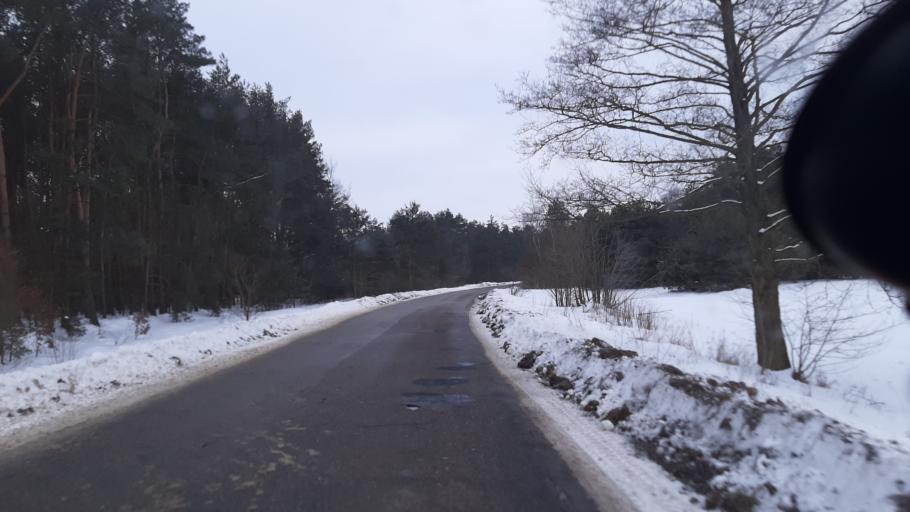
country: PL
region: Lublin Voivodeship
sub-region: Powiat lubartowski
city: Abramow
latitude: 51.4381
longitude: 22.2577
